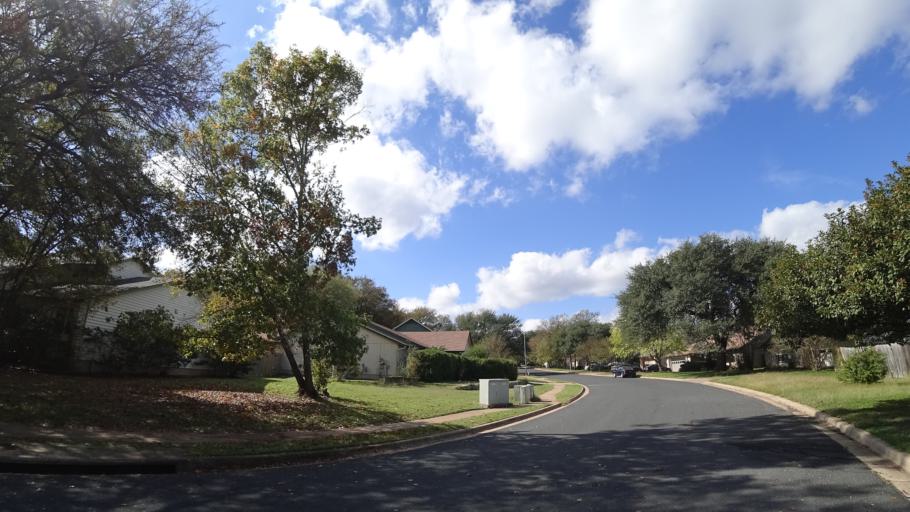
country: US
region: Texas
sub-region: Travis County
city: Wells Branch
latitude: 30.4235
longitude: -97.7233
